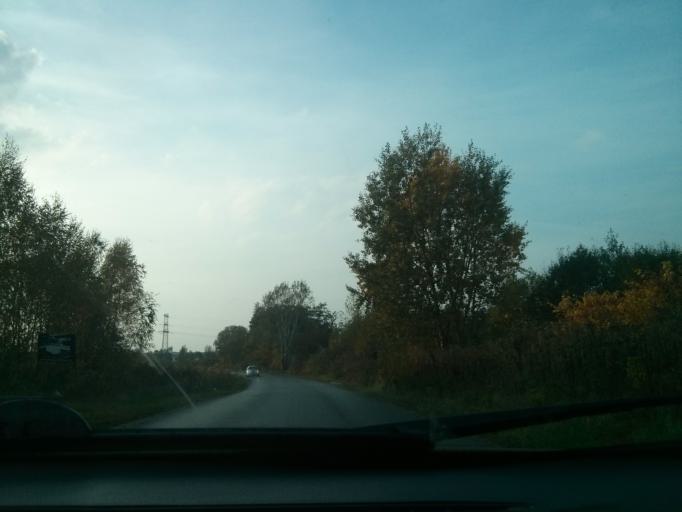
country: PL
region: Masovian Voivodeship
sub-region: Powiat piaseczynski
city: Konstancin-Jeziorna
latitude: 52.1156
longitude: 21.1161
